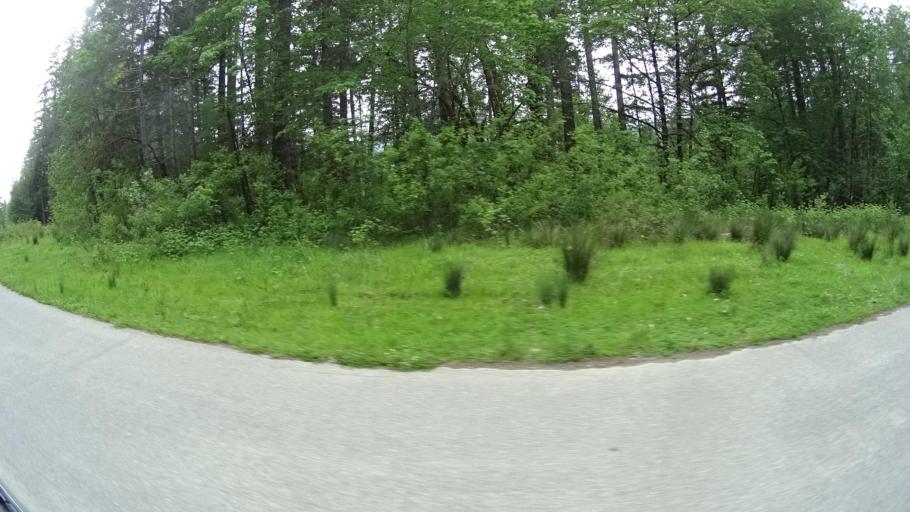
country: US
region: California
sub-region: Humboldt County
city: Willow Creek
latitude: 41.1229
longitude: -123.7429
